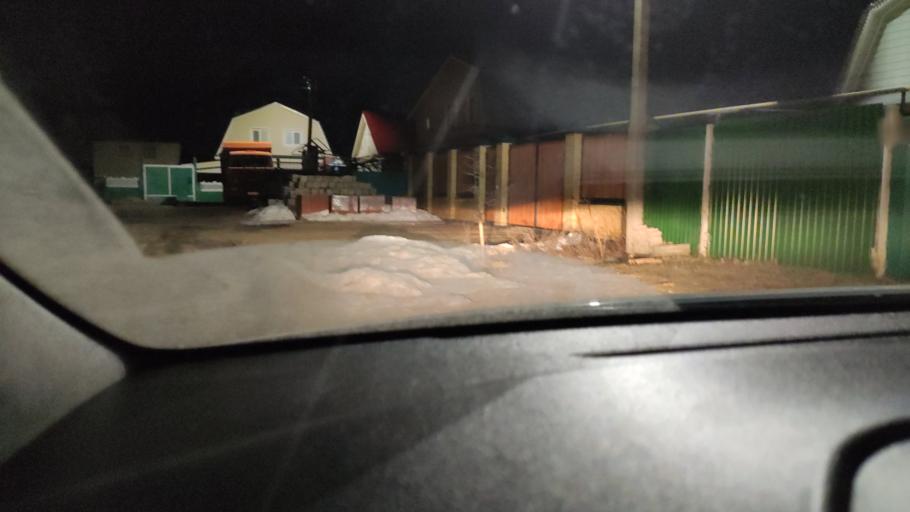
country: RU
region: Tatarstan
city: Staroye Arakchino
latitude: 55.8772
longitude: 49.0406
